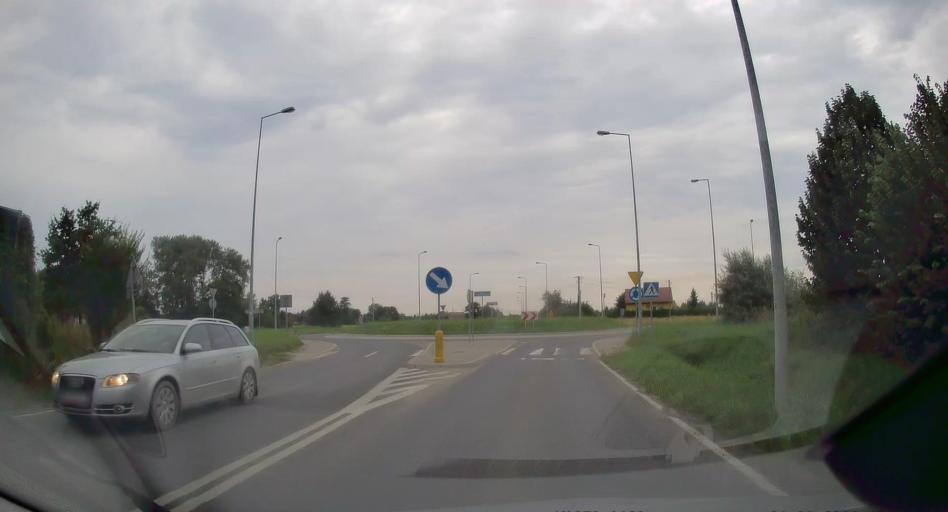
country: PL
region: Lesser Poland Voivodeship
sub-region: Powiat tarnowski
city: Wojnicz
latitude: 49.9736
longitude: 20.8440
